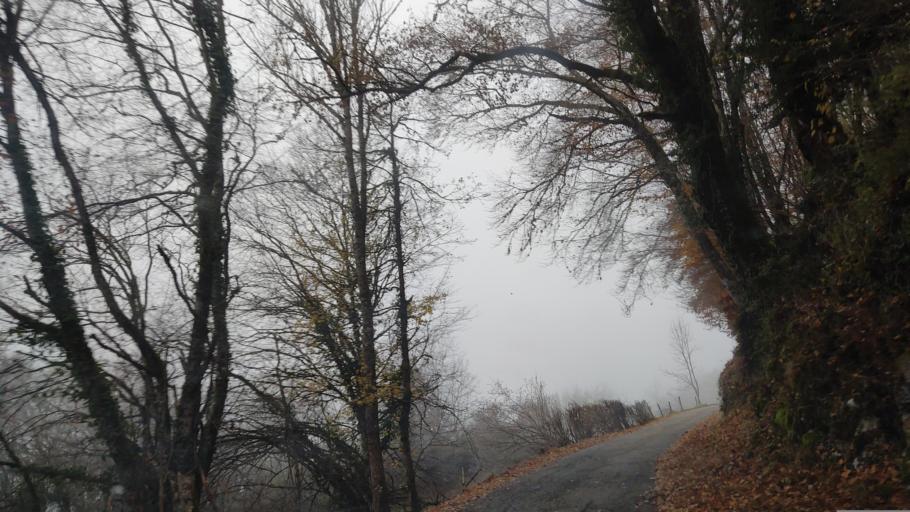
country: FR
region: Rhone-Alpes
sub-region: Departement de la Haute-Savoie
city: Doussard
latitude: 45.6828
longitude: 6.1401
